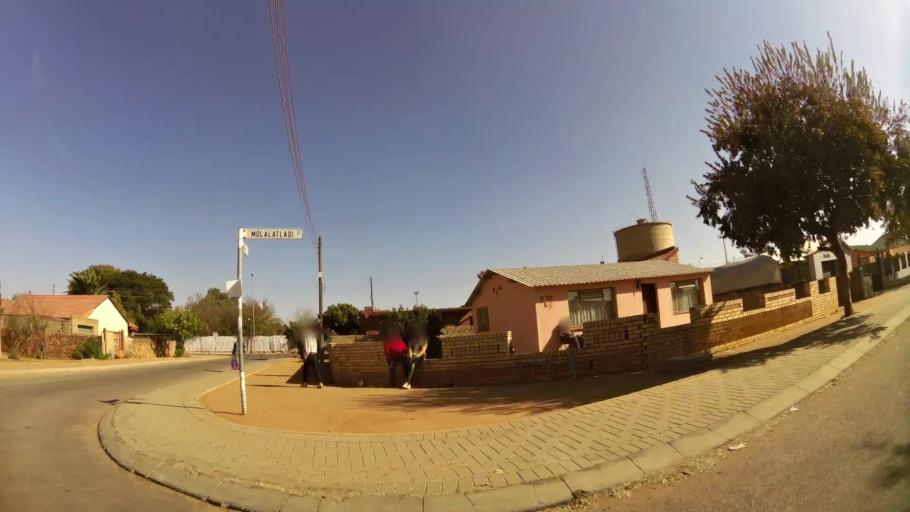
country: ZA
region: Gauteng
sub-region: City of Tshwane Metropolitan Municipality
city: Mabopane
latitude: -25.5357
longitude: 28.0998
